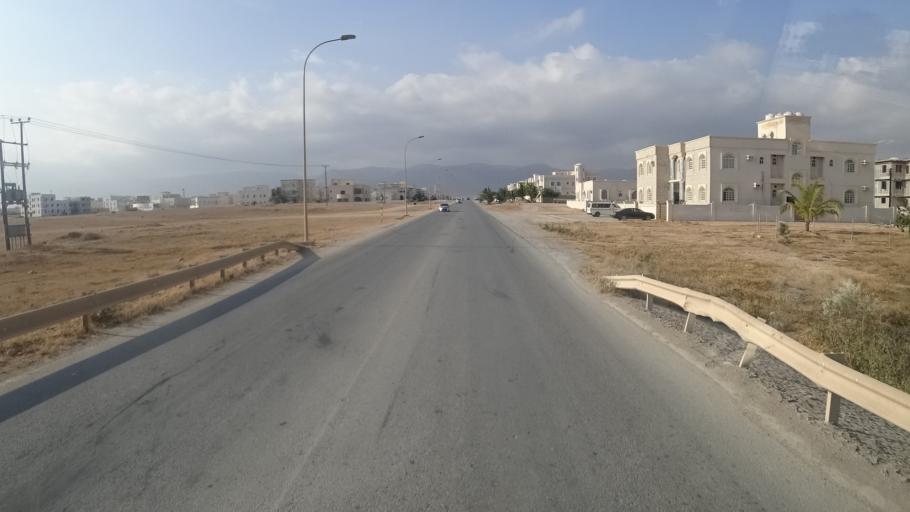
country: OM
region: Zufar
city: Salalah
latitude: 17.0112
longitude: 54.0252
